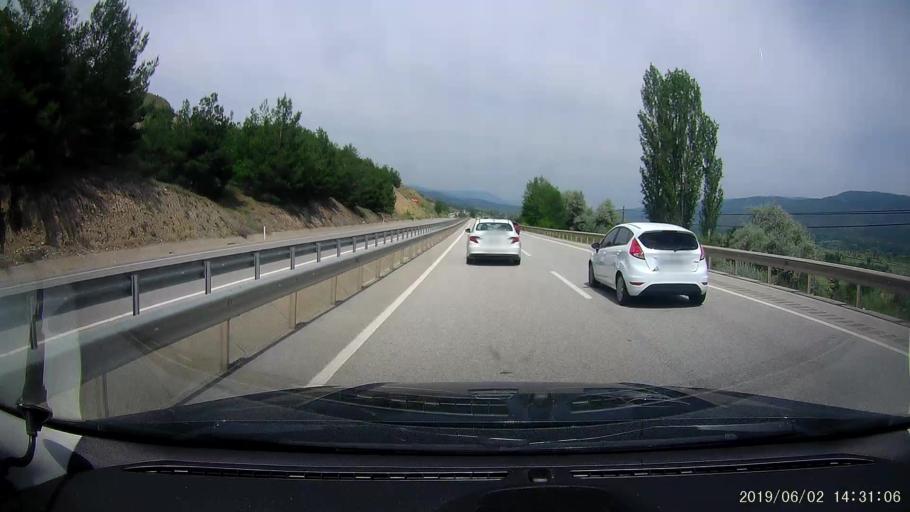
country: TR
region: Kastamonu
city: Tosya
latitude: 41.0152
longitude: 34.1306
